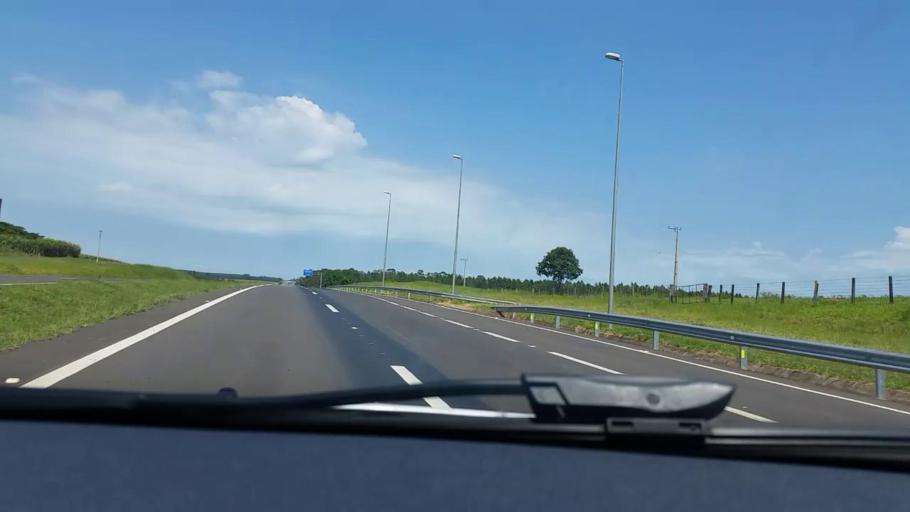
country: BR
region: Sao Paulo
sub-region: Bauru
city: Bauru
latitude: -22.4415
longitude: -49.1489
